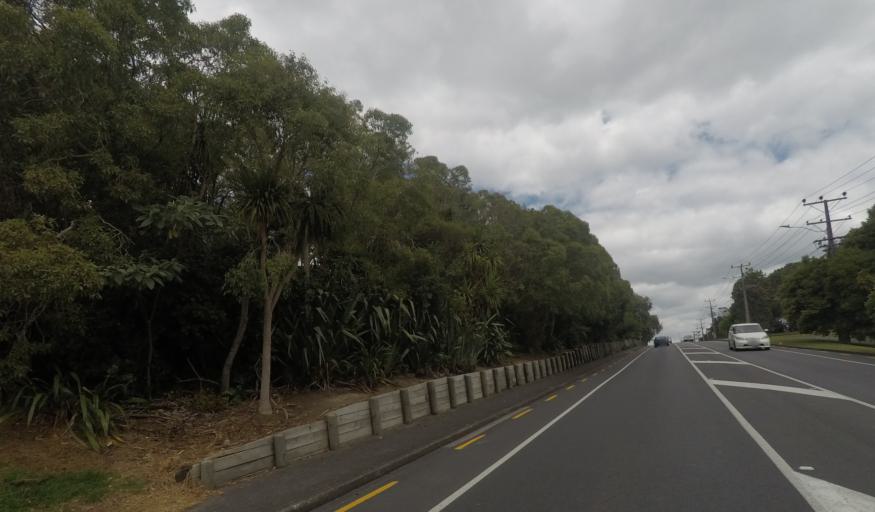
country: NZ
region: Auckland
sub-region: Auckland
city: Rosebank
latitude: -36.8295
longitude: 174.6071
